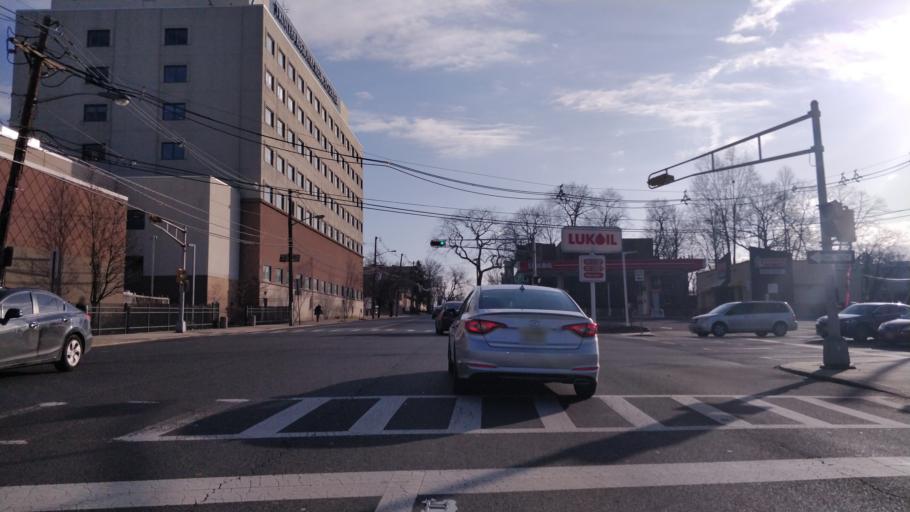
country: US
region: New Jersey
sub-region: Union County
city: Elizabeth
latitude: 40.6599
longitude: -74.2154
